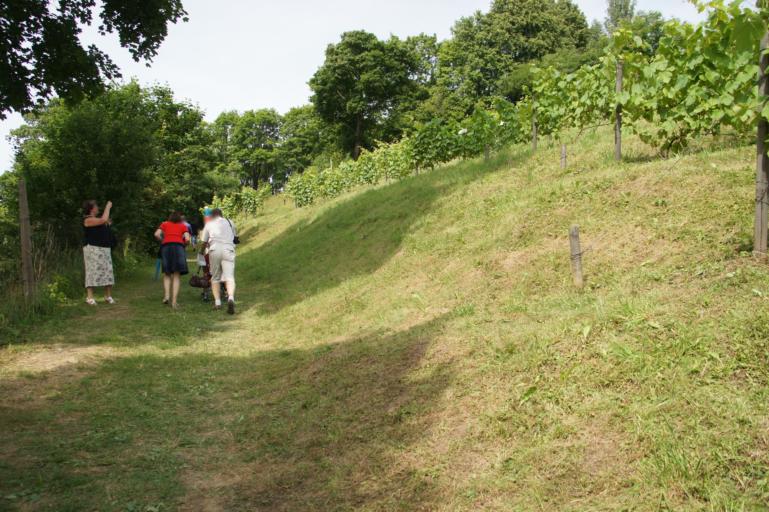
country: LV
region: Talsu Rajons
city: Sabile
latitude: 57.0454
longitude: 22.5764
